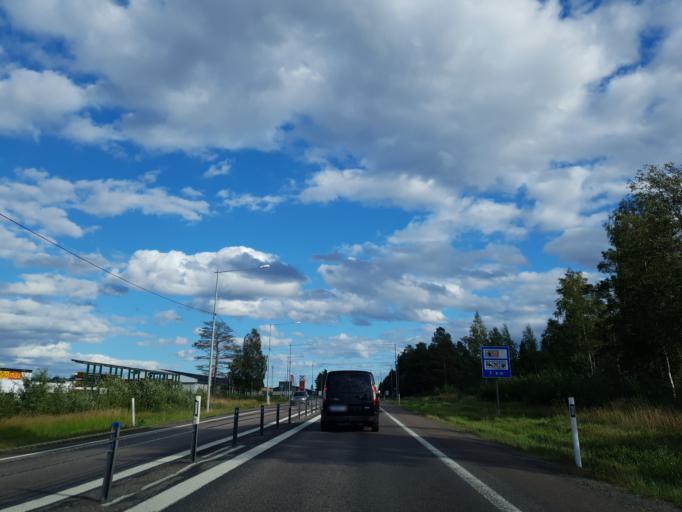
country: SE
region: Vaesternorrland
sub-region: Haernoesands Kommun
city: Haernoesand
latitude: 62.6505
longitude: 17.8917
